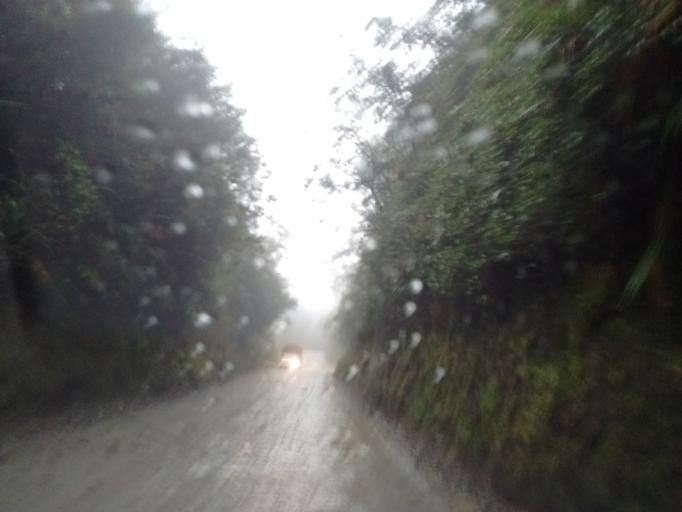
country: CO
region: Cauca
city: Paispamba
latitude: 2.1653
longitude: -76.4131
